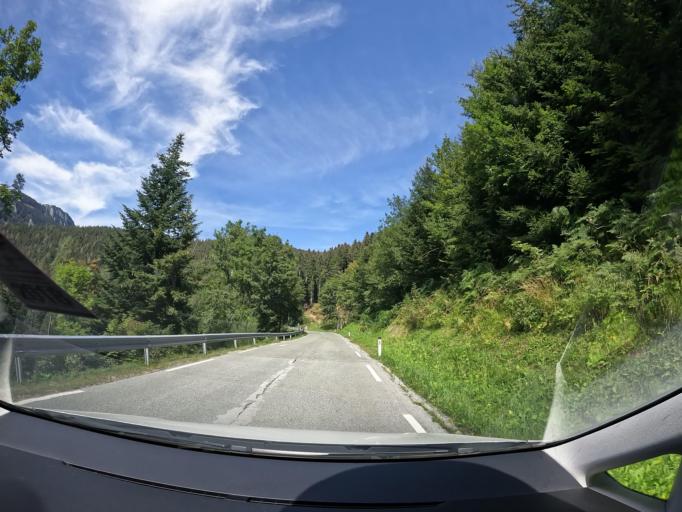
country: AT
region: Carinthia
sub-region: Politischer Bezirk Sankt Veit an der Glan
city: Liebenfels
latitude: 46.7145
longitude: 14.2568
